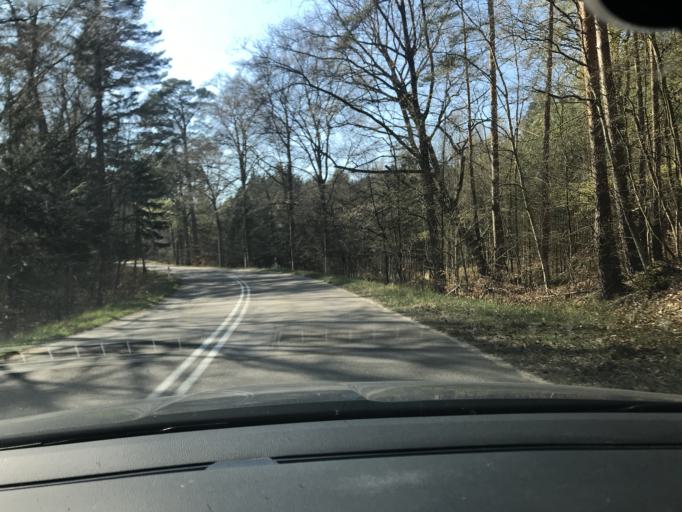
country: PL
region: Pomeranian Voivodeship
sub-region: Powiat nowodworski
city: Krynica Morska
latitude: 54.3642
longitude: 19.3658
